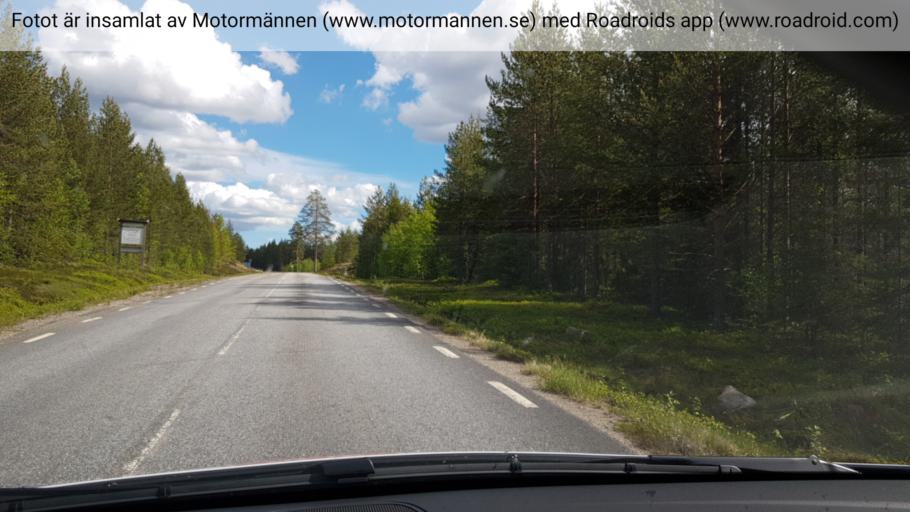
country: SE
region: Vaesterbotten
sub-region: Umea Kommun
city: Ersmark
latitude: 64.2422
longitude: 20.2642
